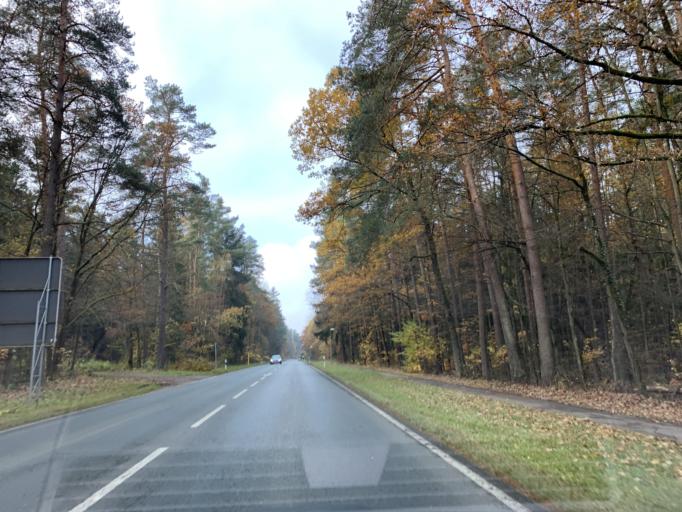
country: DE
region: Bavaria
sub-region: Upper Palatinate
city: Bodenwohr
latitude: 49.2742
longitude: 12.3273
